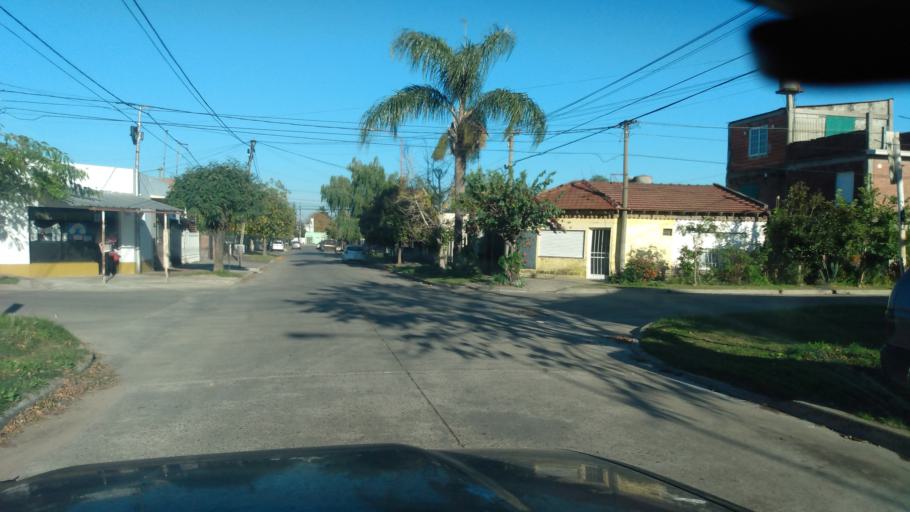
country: AR
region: Buenos Aires
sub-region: Partido de Lujan
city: Lujan
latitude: -34.5608
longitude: -59.0978
